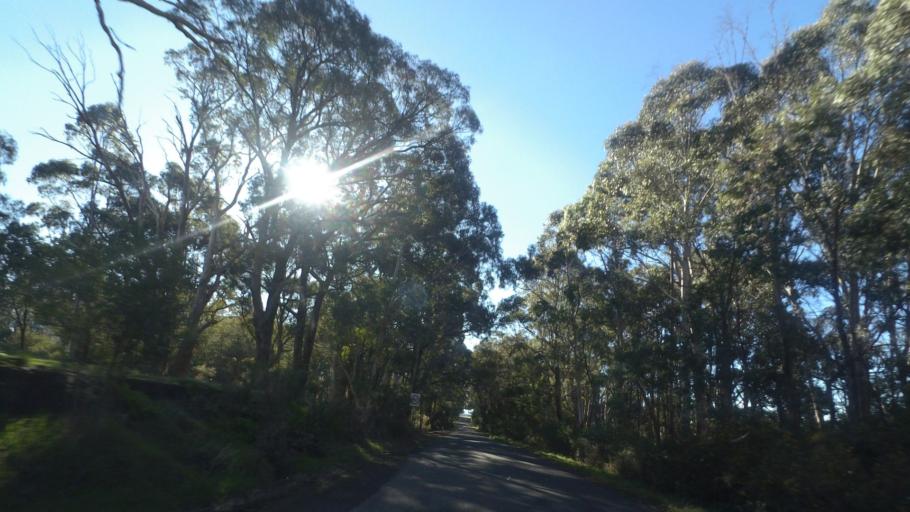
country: AU
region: Victoria
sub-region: Mount Alexander
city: Castlemaine
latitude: -37.3066
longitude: 144.3301
